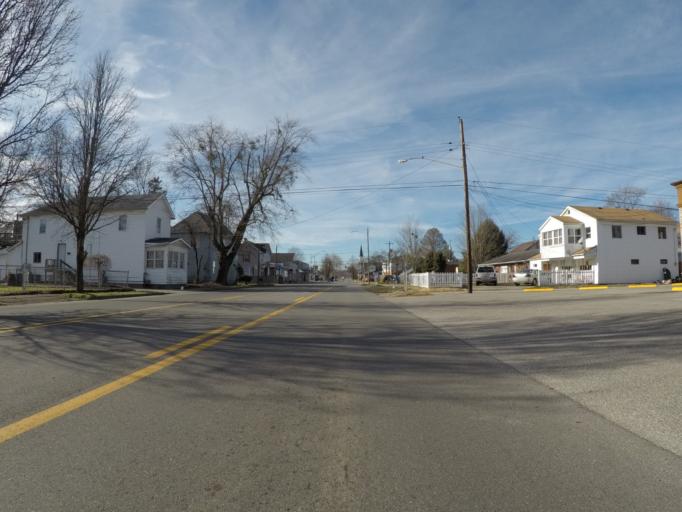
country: US
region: West Virginia
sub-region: Wayne County
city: Ceredo
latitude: 38.3963
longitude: -82.5570
